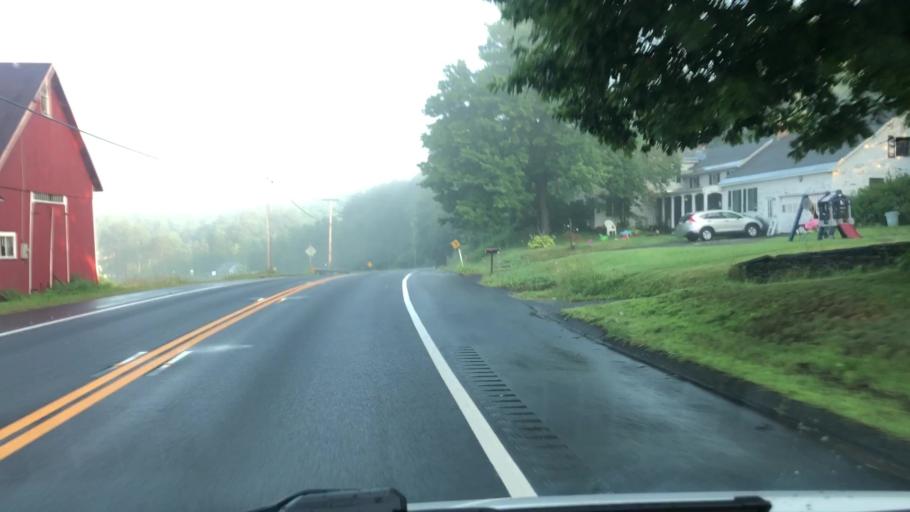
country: US
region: Massachusetts
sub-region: Hampshire County
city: Chesterfield
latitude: 42.4555
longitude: -72.8288
